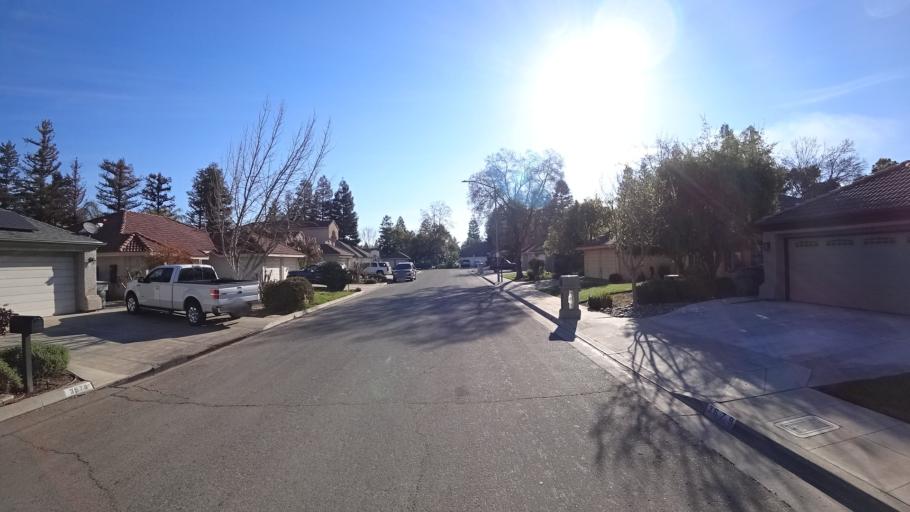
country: US
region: California
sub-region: Fresno County
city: West Park
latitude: 36.8287
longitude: -119.8600
